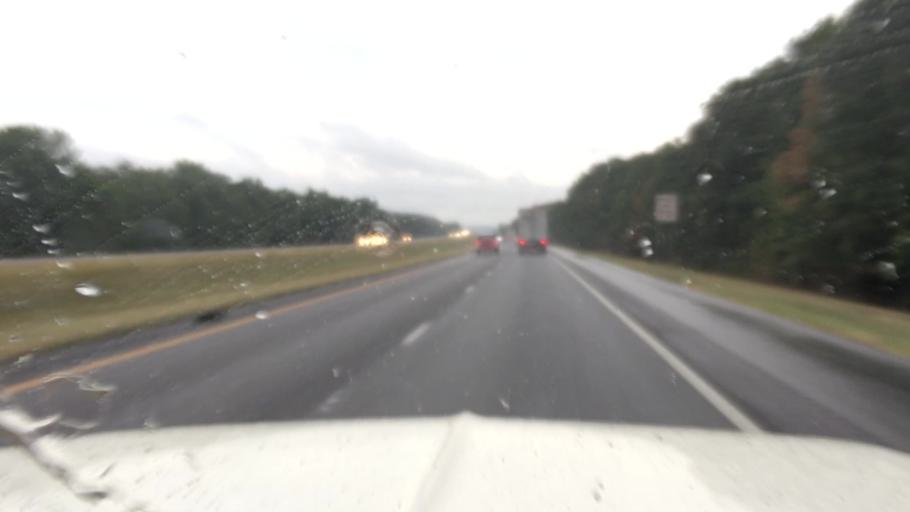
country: US
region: Alabama
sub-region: Morgan County
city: Falkville
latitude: 34.4033
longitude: -86.8979
